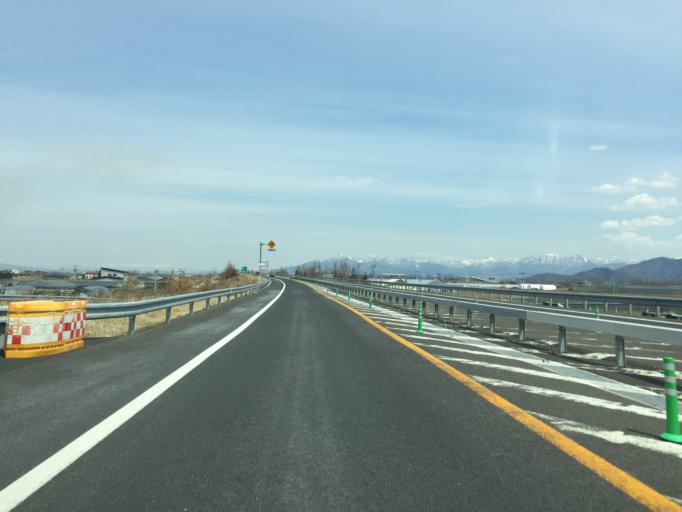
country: JP
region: Yamagata
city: Tendo
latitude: 38.3188
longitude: 140.3240
